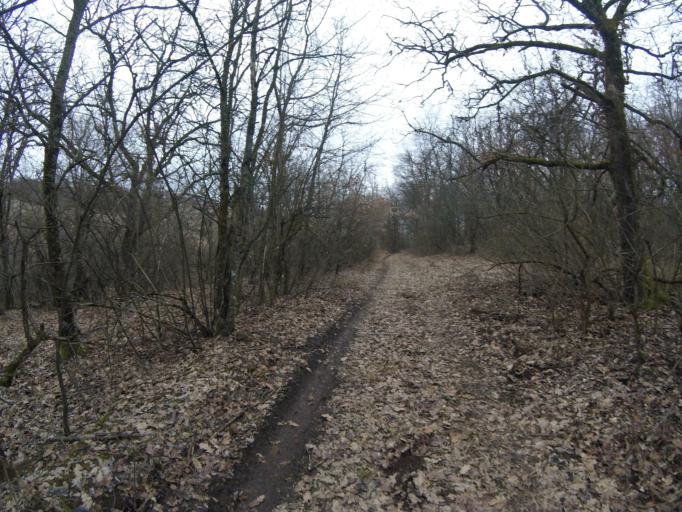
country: HU
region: Borsod-Abauj-Zemplen
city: Rudabanya
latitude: 48.4543
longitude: 20.6084
